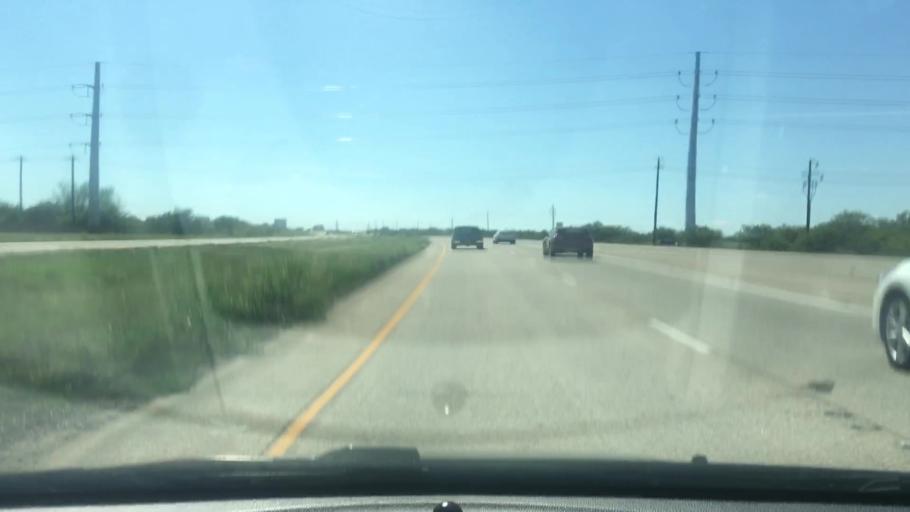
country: US
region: Texas
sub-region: Denton County
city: Denton
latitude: 33.2604
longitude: -97.1354
